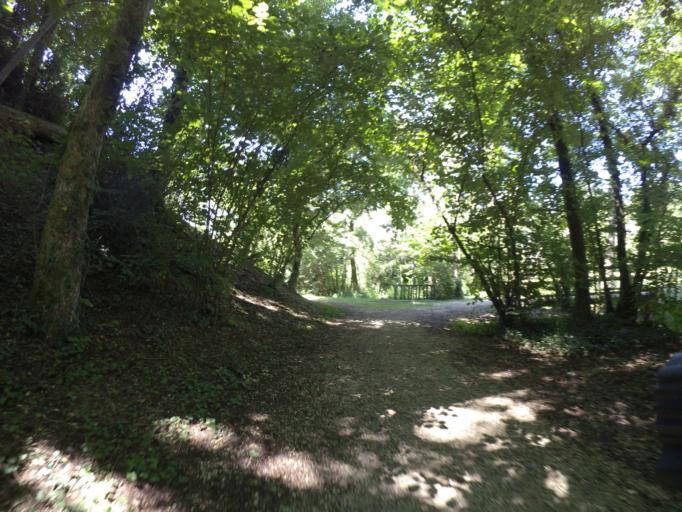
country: IT
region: Friuli Venezia Giulia
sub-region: Provincia di Udine
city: Teor
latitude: 45.8745
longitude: 13.0798
